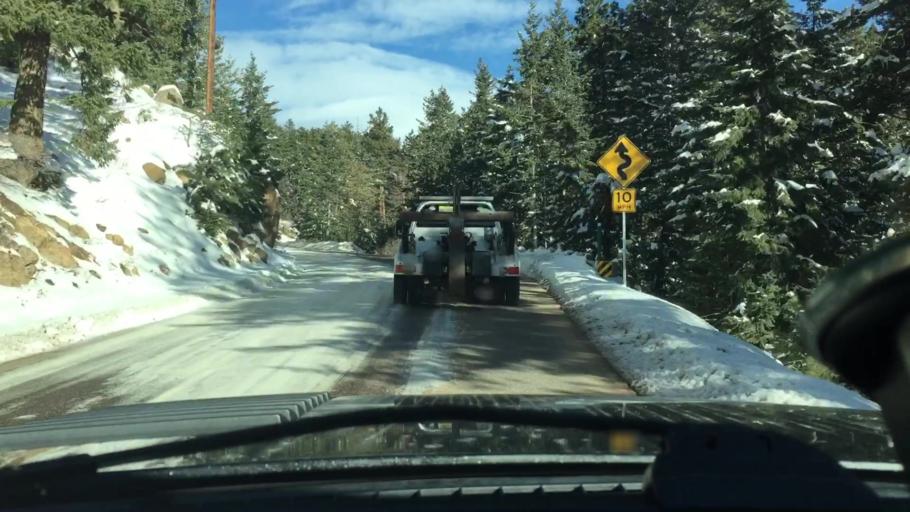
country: US
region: Colorado
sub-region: Jefferson County
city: Indian Hills
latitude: 39.5551
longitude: -105.2452
